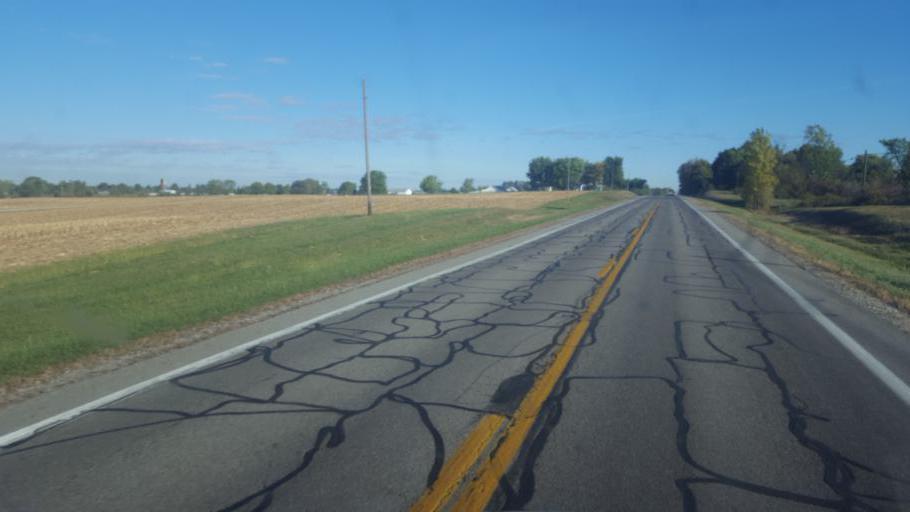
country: US
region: Ohio
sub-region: Crawford County
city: Galion
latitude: 40.6551
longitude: -82.8218
